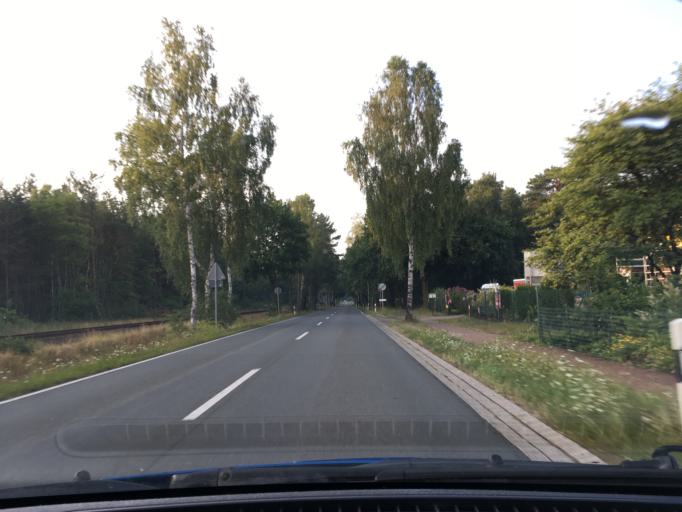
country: DE
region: Lower Saxony
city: Celle
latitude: 52.7073
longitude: 10.0807
